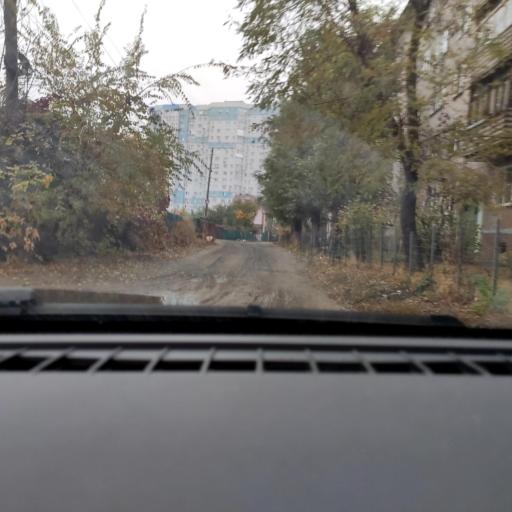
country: RU
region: Voronezj
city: Voronezh
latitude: 51.6518
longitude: 39.2372
